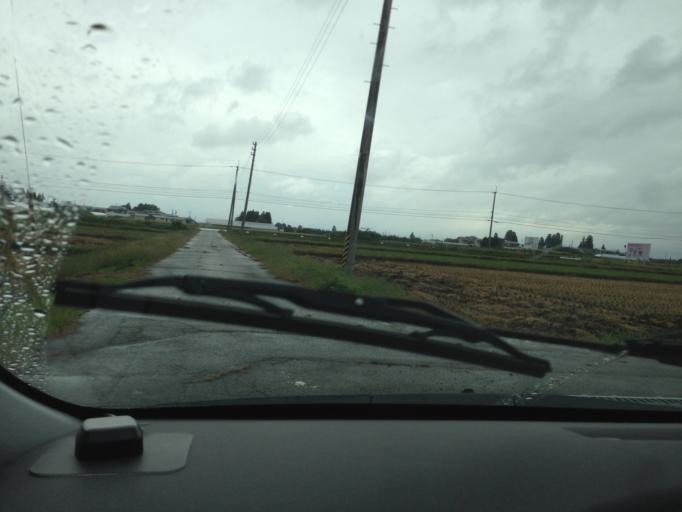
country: JP
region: Fukushima
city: Kitakata
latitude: 37.4696
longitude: 139.8667
